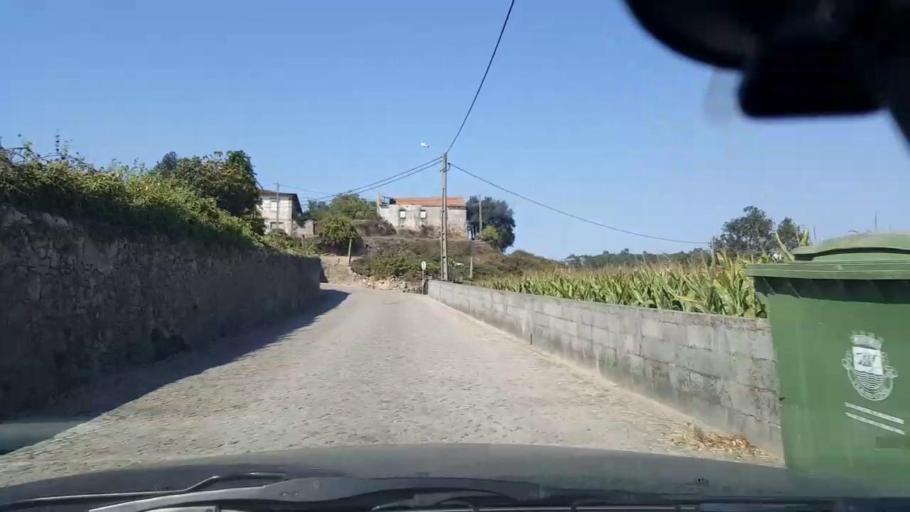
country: PT
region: Porto
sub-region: Povoa de Varzim
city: Pedroso
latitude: 41.3996
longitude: -8.6887
